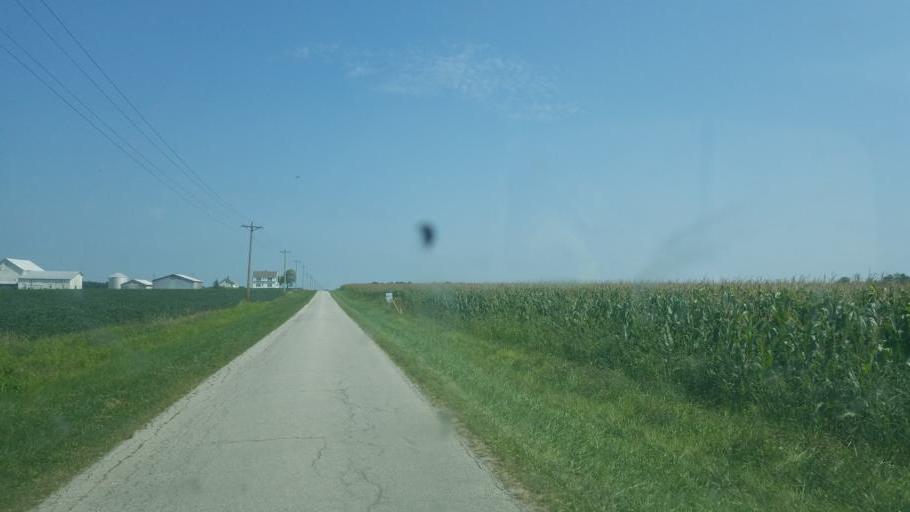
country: US
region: Ohio
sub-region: Crawford County
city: Bucyrus
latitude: 40.9358
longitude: -83.0329
